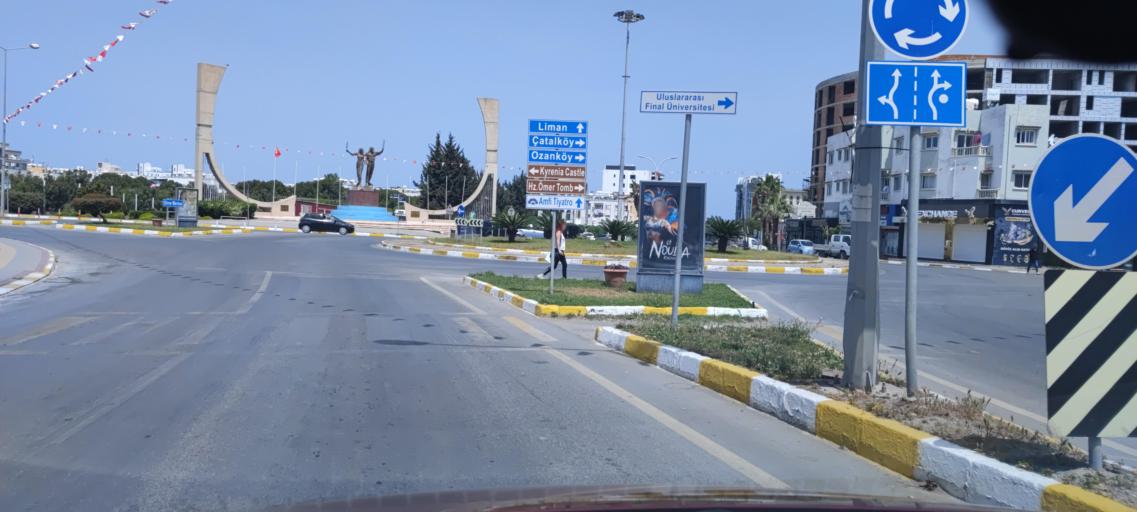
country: CY
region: Keryneia
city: Kyrenia
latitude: 35.3337
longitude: 33.3309
